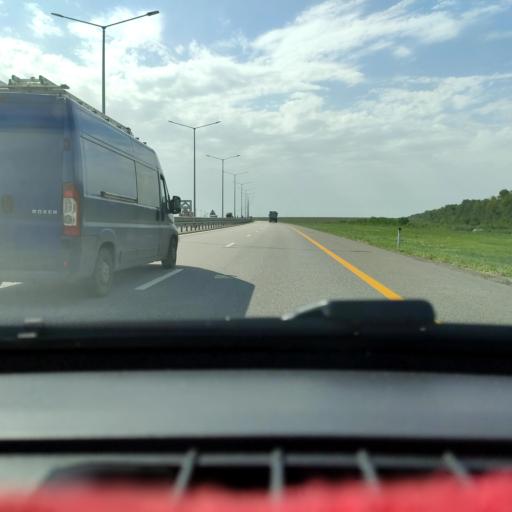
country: RU
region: Voronezj
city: Podkletnoye
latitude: 51.5152
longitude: 39.5116
